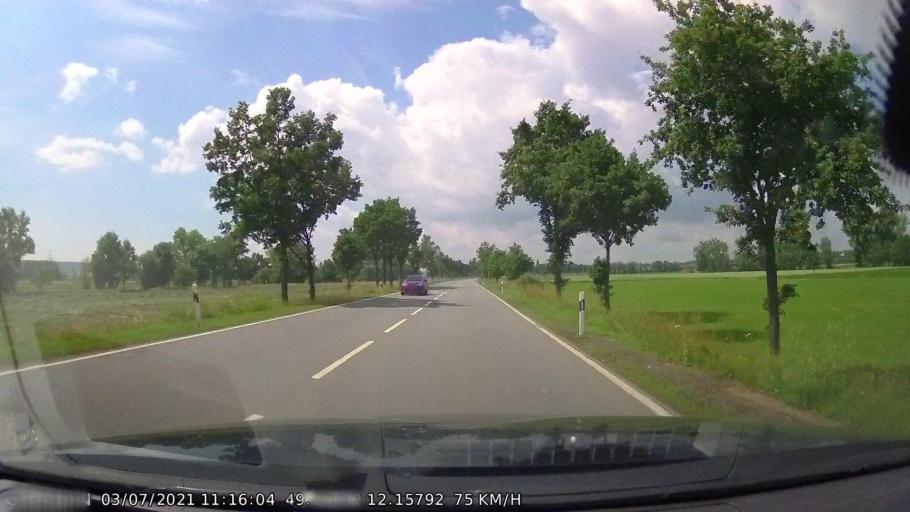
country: DE
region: Bavaria
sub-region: Upper Palatinate
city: Schirmitz
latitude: 49.6548
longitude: 12.1579
